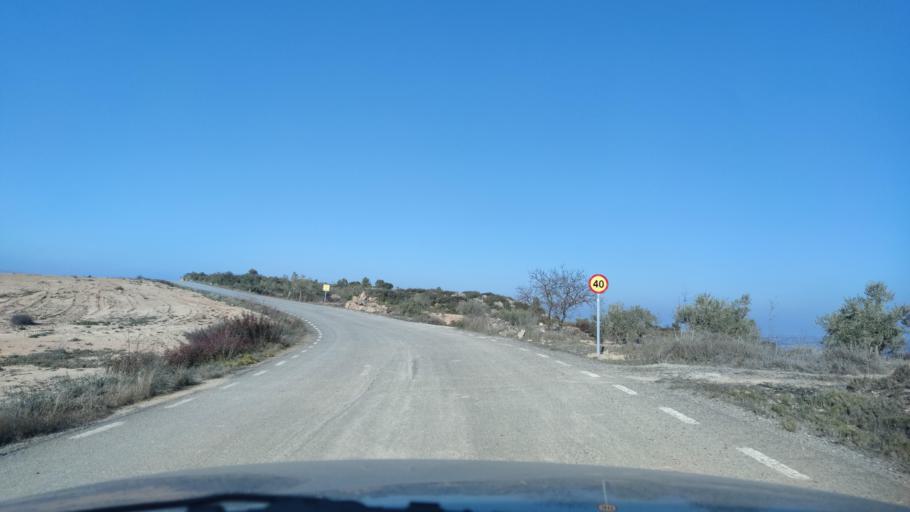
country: ES
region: Catalonia
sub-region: Provincia de Lleida
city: Torrebesses
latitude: 41.4197
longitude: 0.5717
